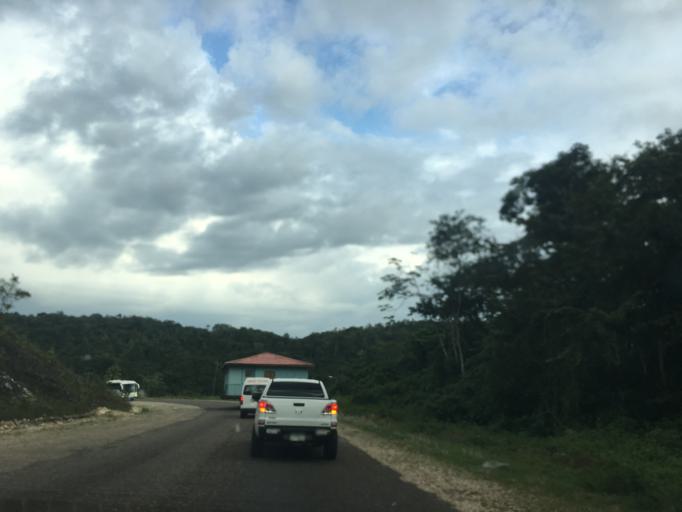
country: BZ
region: Cayo
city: San Ignacio
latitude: 17.2029
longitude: -88.9472
